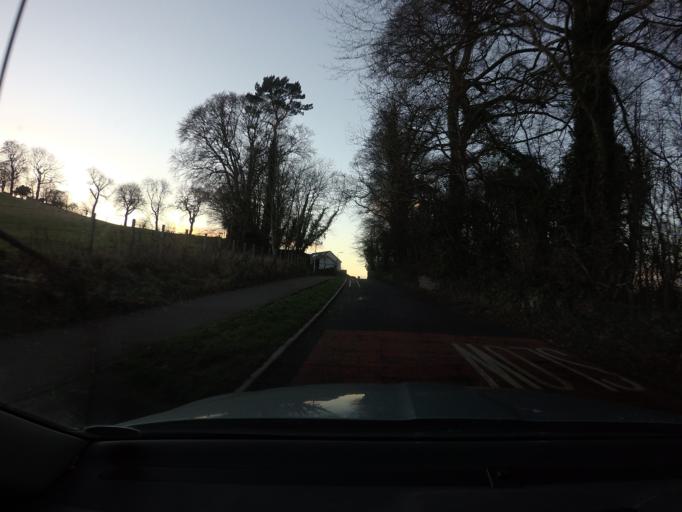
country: GB
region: Scotland
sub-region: Fife
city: Newport-On-Tay
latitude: 56.4332
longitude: -2.9431
